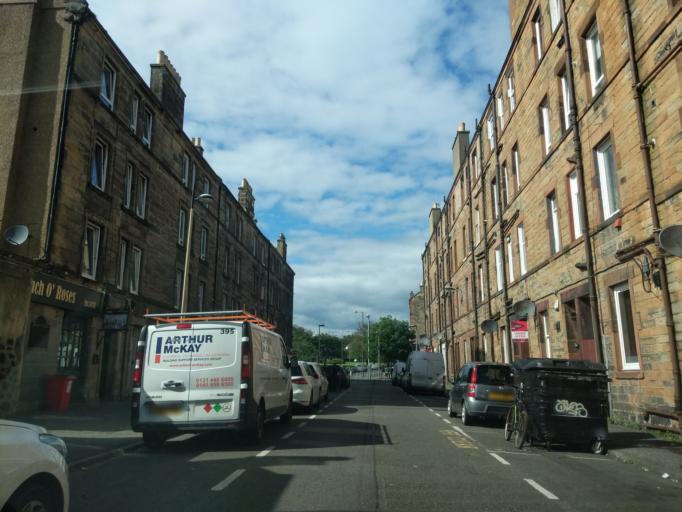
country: GB
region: Scotland
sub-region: West Lothian
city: Seafield
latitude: 55.9590
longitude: -3.1497
